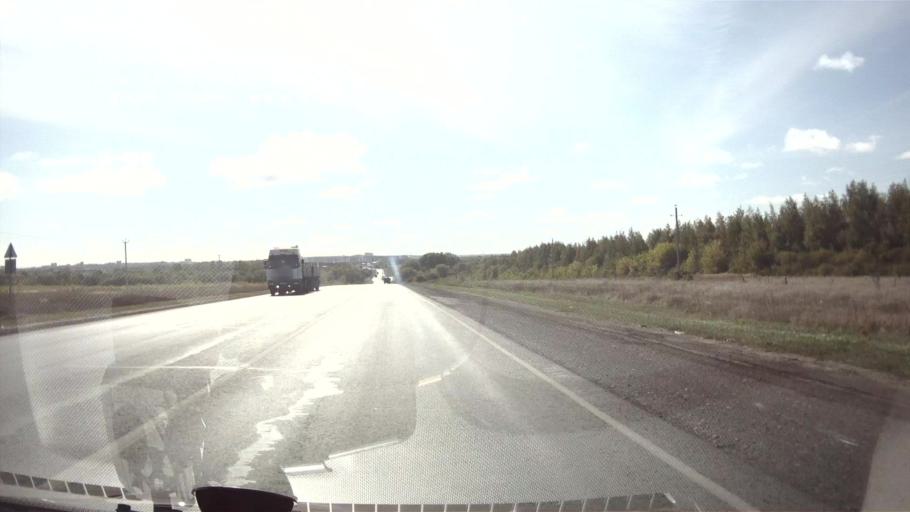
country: RU
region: Ulyanovsk
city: Isheyevka
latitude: 54.3101
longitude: 48.2370
